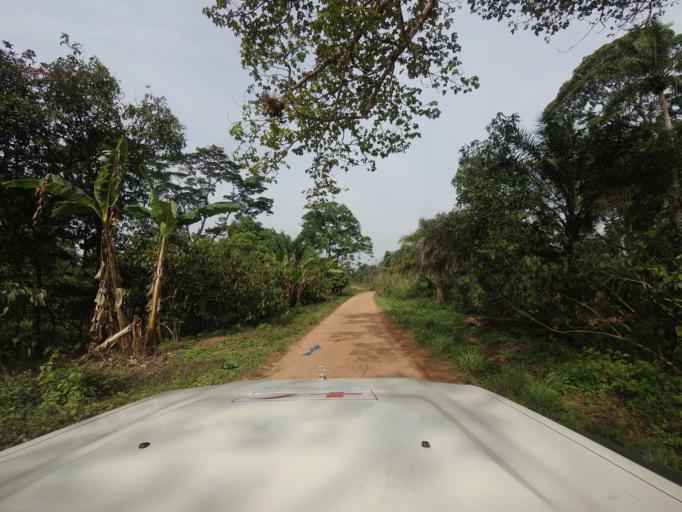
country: GN
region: Nzerekore
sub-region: Macenta
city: Macenta
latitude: 8.5231
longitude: -9.5099
